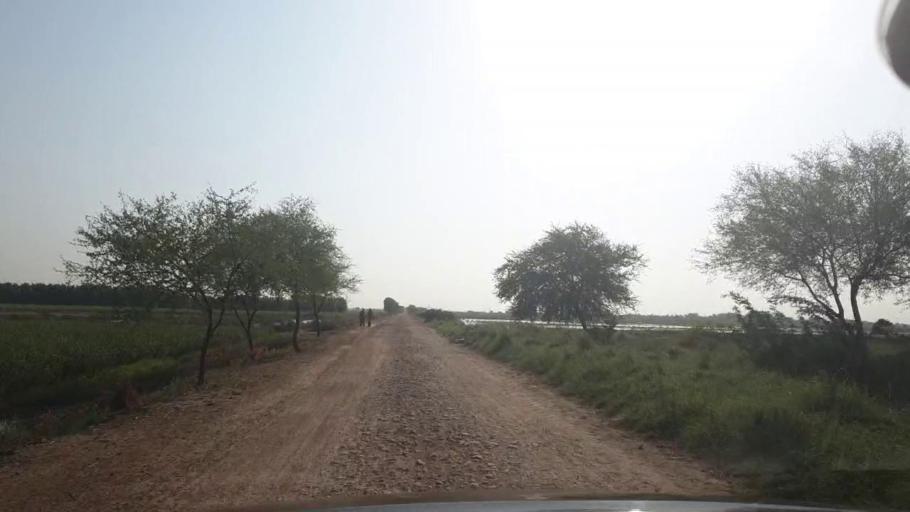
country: PK
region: Sindh
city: Tando Bago
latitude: 24.6510
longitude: 69.1411
